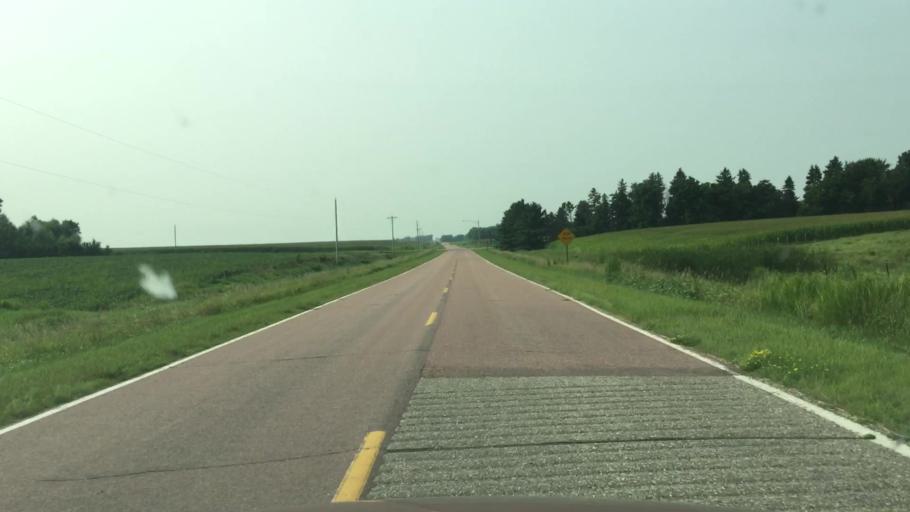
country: US
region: Iowa
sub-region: O'Brien County
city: Sheldon
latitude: 43.2469
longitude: -95.7833
